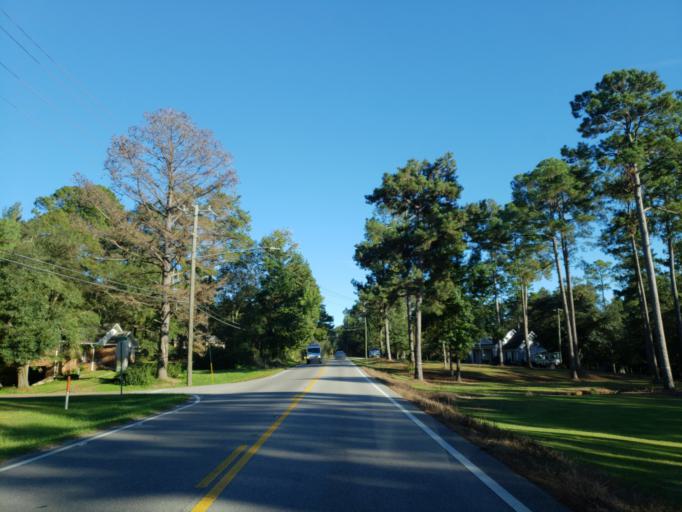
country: US
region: Mississippi
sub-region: Perry County
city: Richton
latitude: 31.3506
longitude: -88.9488
